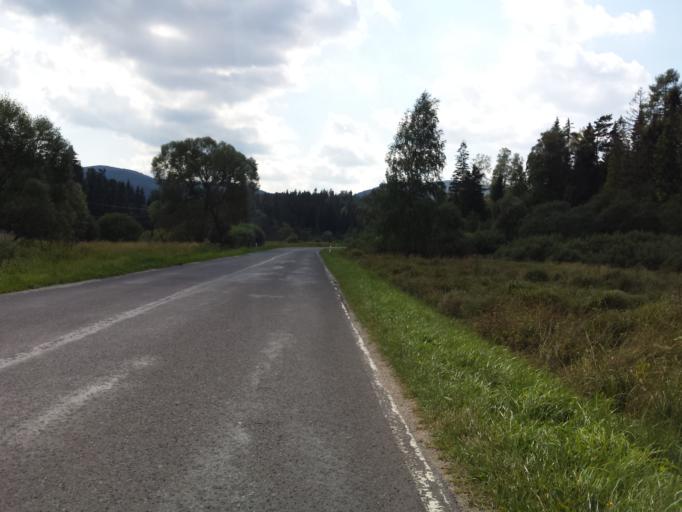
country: PL
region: Subcarpathian Voivodeship
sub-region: Powiat leski
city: Cisna
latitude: 49.1882
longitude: 22.4197
